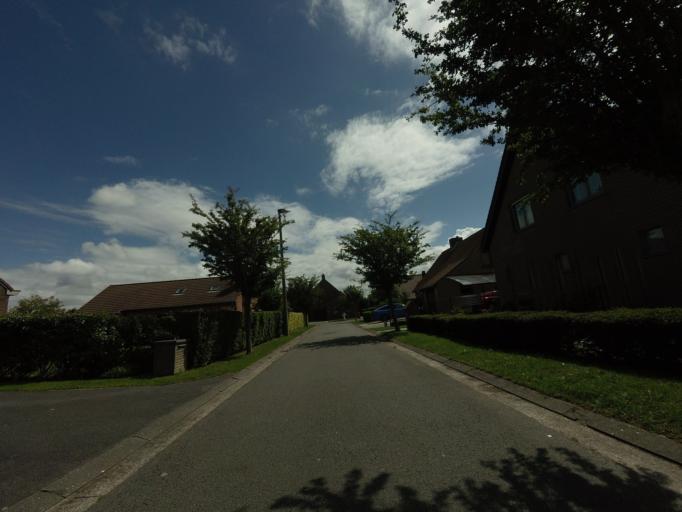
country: BE
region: Flanders
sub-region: Provincie West-Vlaanderen
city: Bredene
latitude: 51.2392
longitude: 2.9519
